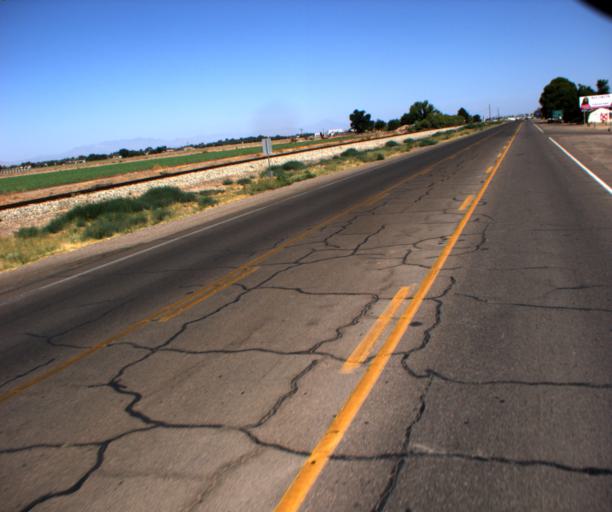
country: US
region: Arizona
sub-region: Graham County
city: Safford
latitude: 32.8221
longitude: -109.6877
